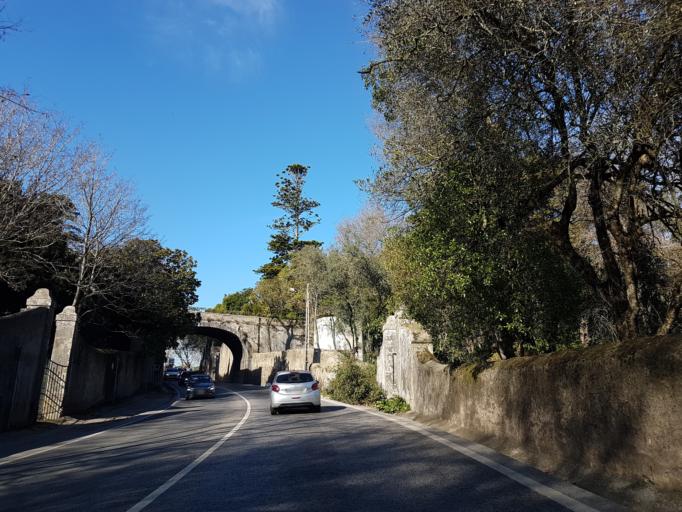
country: PT
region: Lisbon
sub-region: Sintra
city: Sintra
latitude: 38.7864
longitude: -9.3717
